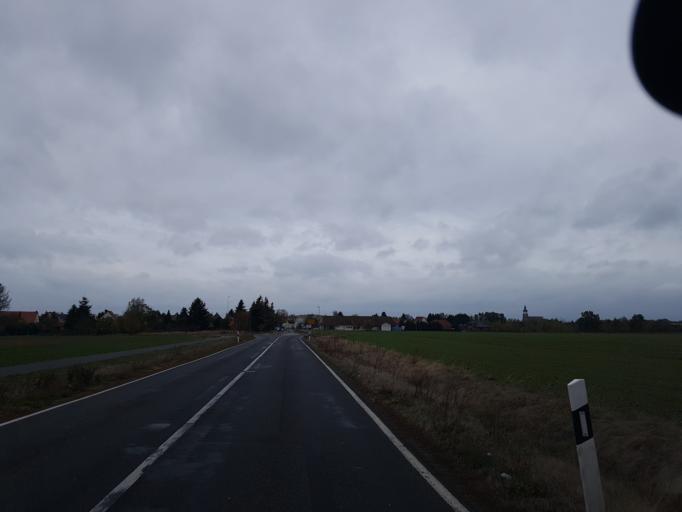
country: DE
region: Brandenburg
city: Herzberg
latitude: 51.6804
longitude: 13.2298
